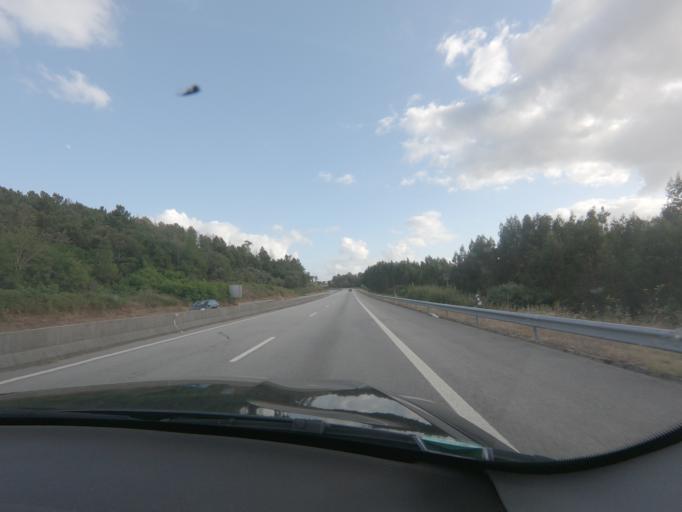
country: PT
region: Viseu
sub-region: Viseu
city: Abraveses
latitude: 40.6527
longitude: -7.9668
